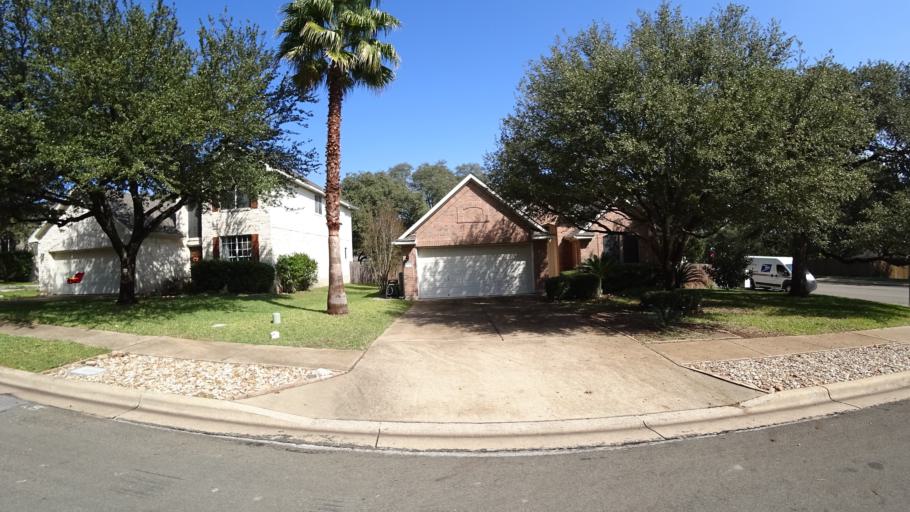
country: US
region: Texas
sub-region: Travis County
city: Shady Hollow
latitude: 30.2084
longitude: -97.8716
